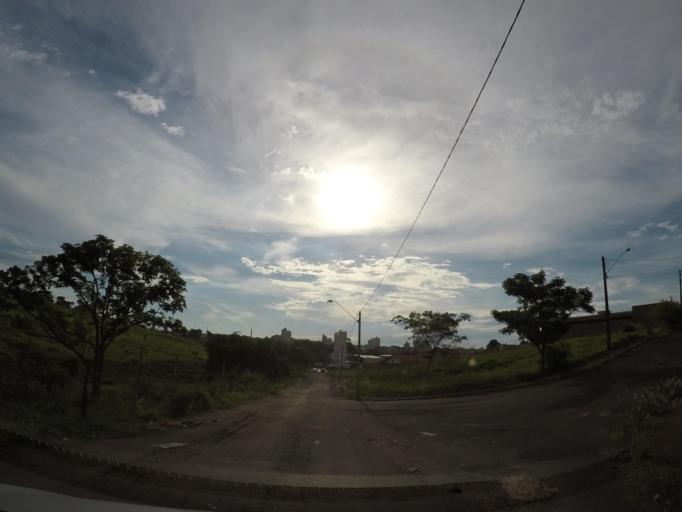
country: BR
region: Sao Paulo
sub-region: Sumare
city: Sumare
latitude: -22.8235
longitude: -47.2526
